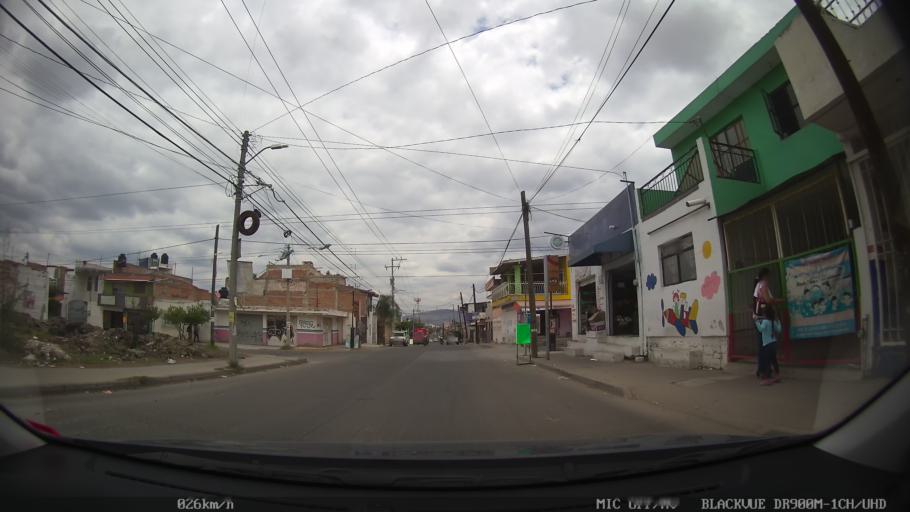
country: MX
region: Jalisco
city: Tonala
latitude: 20.6462
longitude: -103.2535
